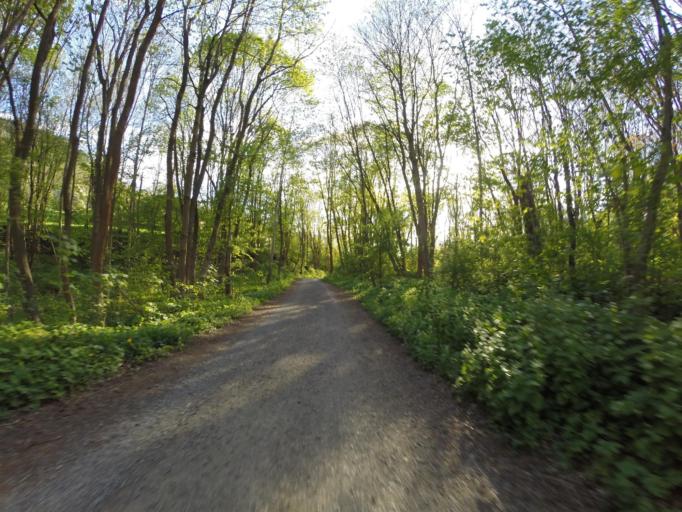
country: DE
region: Thuringia
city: Jena
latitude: 50.9066
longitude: 11.6172
